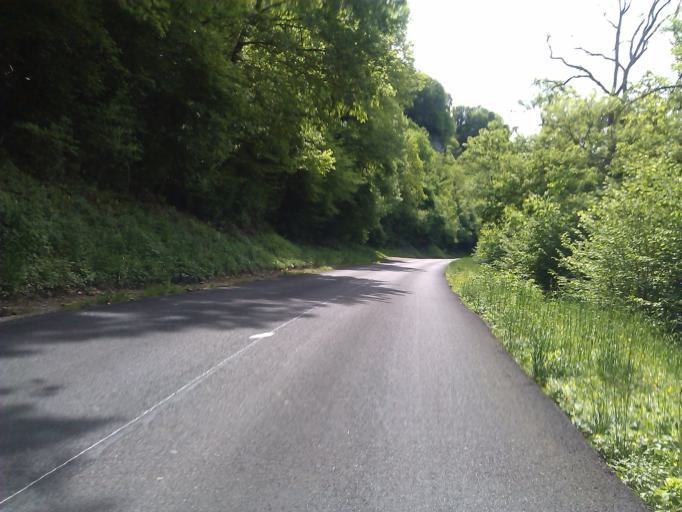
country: FR
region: Franche-Comte
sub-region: Departement du Doubs
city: Boussieres
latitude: 47.1646
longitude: 5.9019
